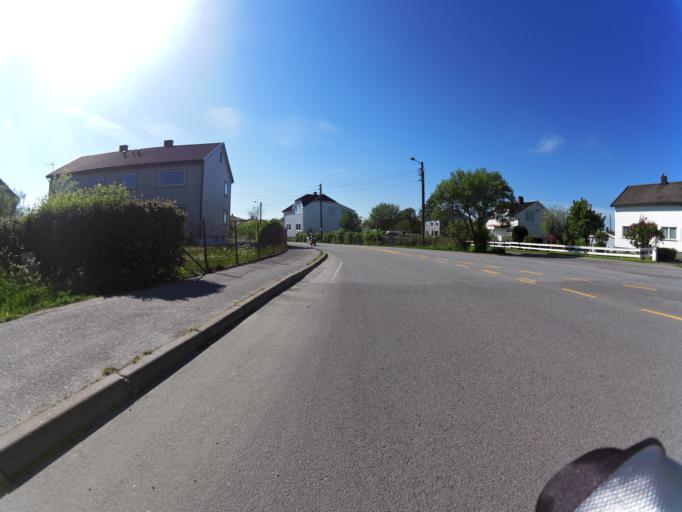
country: NO
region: Ostfold
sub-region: Fredrikstad
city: Fredrikstad
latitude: 59.2315
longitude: 11.0007
